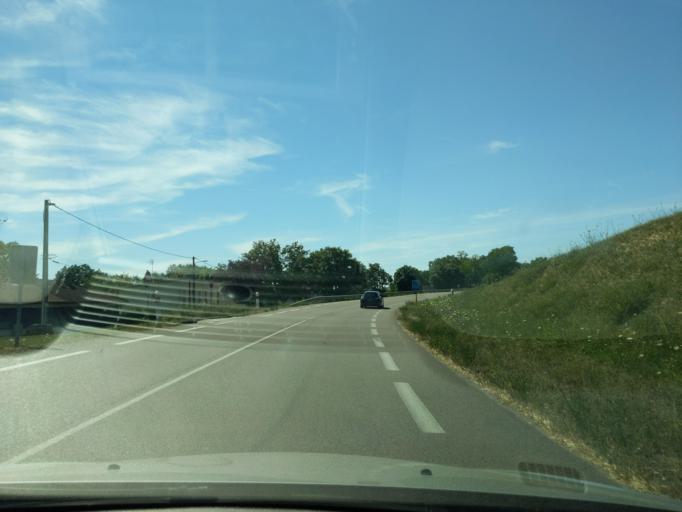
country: FR
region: Bourgogne
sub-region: Departement de la Cote-d'Or
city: Neuilly-les-Dijon
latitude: 47.2833
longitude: 5.1022
